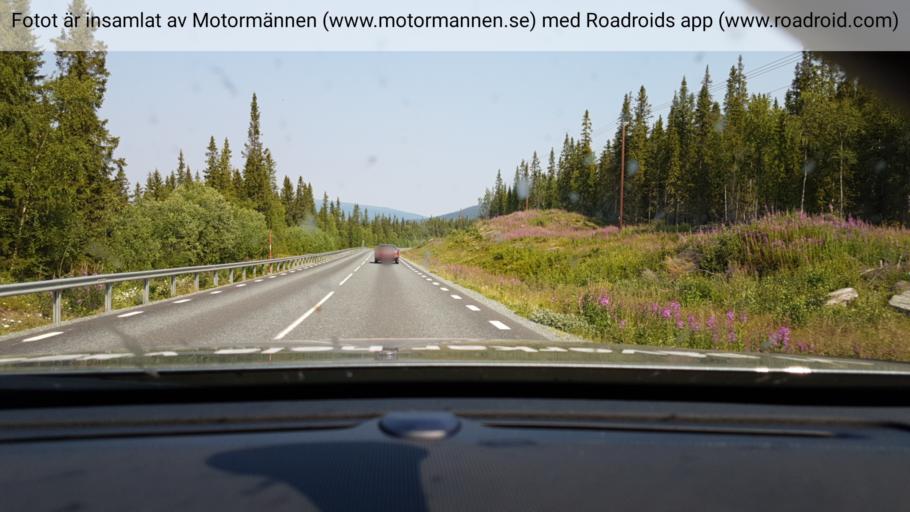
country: SE
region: Vaesterbotten
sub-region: Vilhelmina Kommun
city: Sjoberg
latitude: 65.6086
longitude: 15.5331
